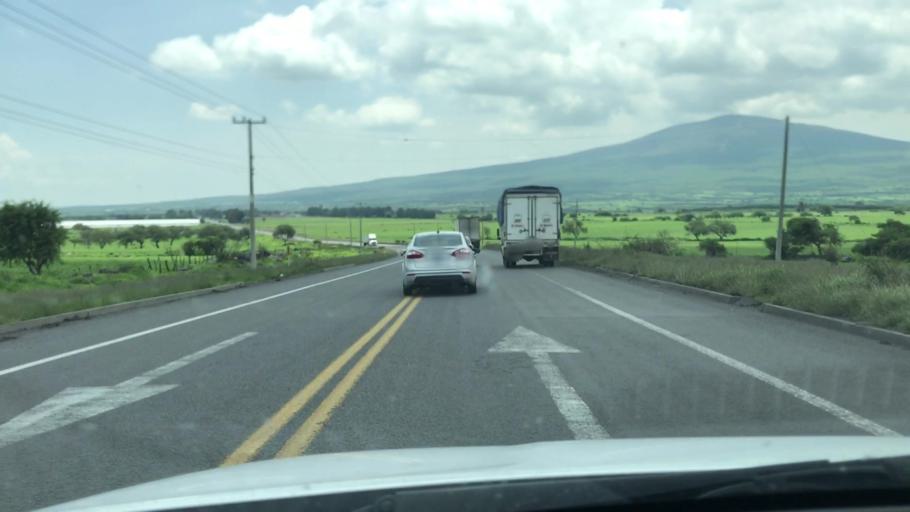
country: MX
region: Michoacan
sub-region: Yurecuaro
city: Yurecuaro
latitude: 20.3380
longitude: -102.1921
